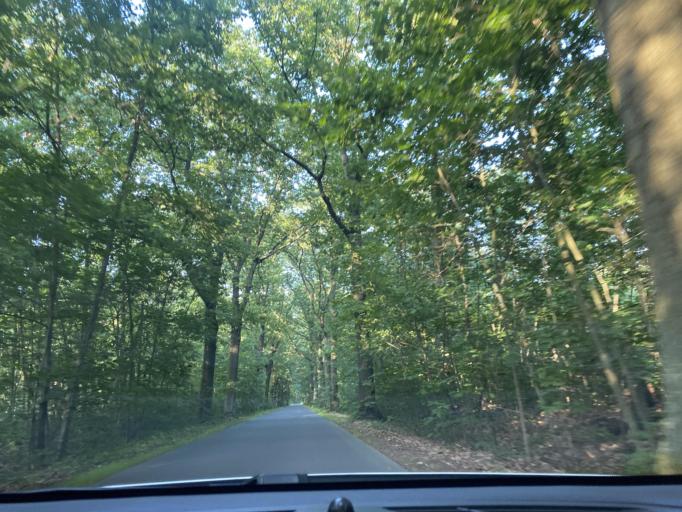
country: DE
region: Saxony
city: Niesky
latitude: 51.2648
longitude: 14.8008
